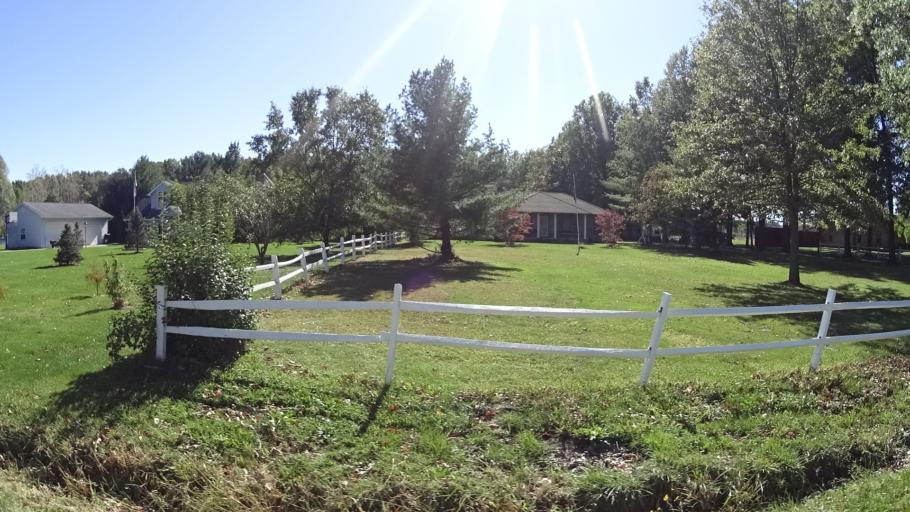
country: US
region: Ohio
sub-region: Lorain County
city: Oberlin
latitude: 41.2794
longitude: -82.1985
